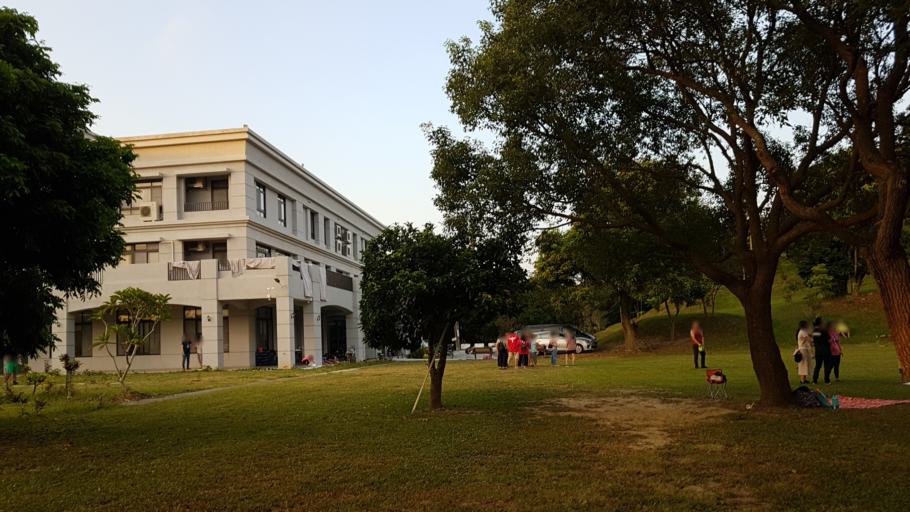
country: TW
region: Taiwan
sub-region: Chiayi
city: Jiayi Shi
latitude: 23.3586
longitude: 120.4674
